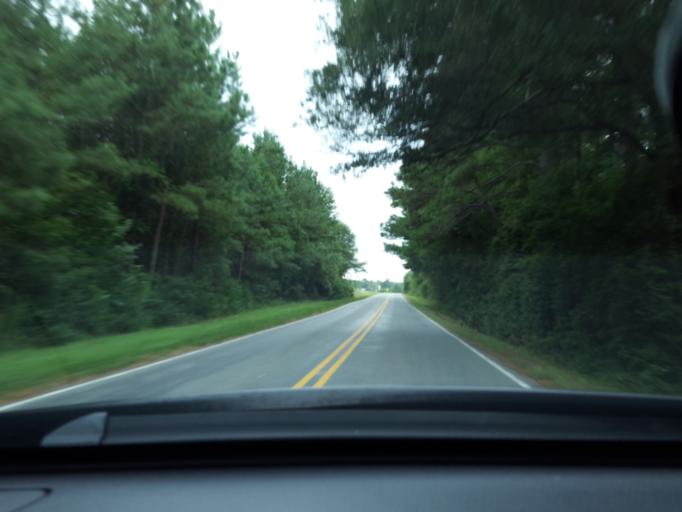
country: US
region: North Carolina
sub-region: Sampson County
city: Roseboro
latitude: 34.7866
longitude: -78.3755
